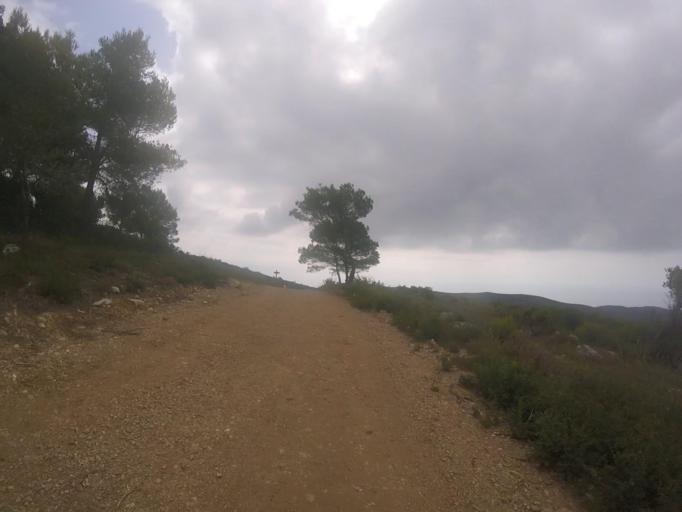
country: ES
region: Valencia
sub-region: Provincia de Castello
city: Santa Magdalena de Pulpis
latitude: 40.3494
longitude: 0.3325
